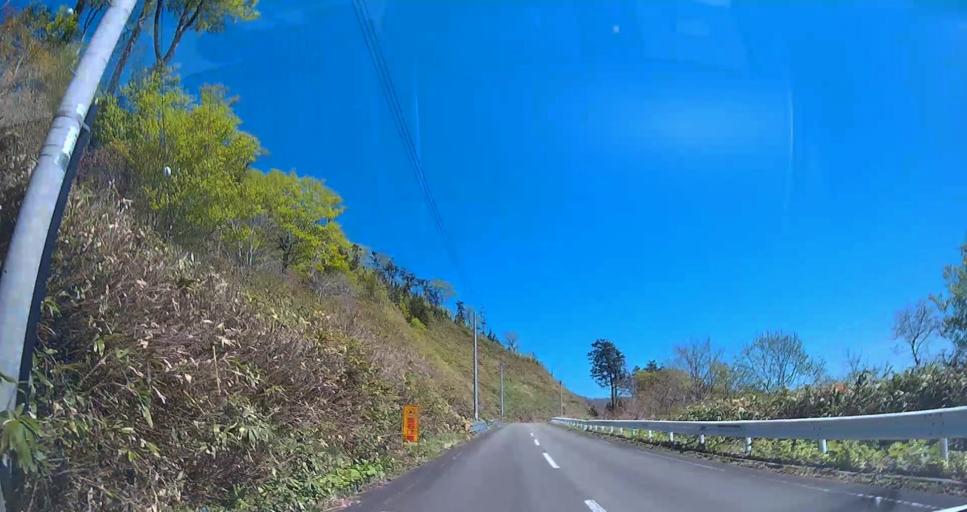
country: JP
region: Aomori
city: Aomori Shi
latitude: 41.2246
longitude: 140.8043
